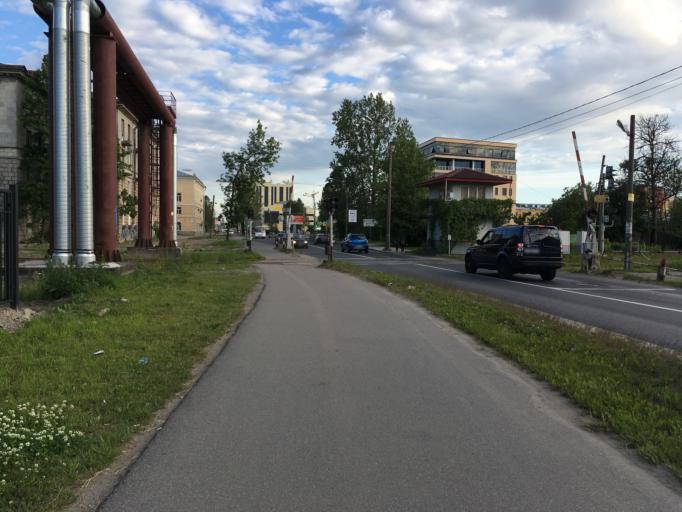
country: RU
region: St.-Petersburg
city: Krasnogvargeisky
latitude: 59.9416
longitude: 30.4351
